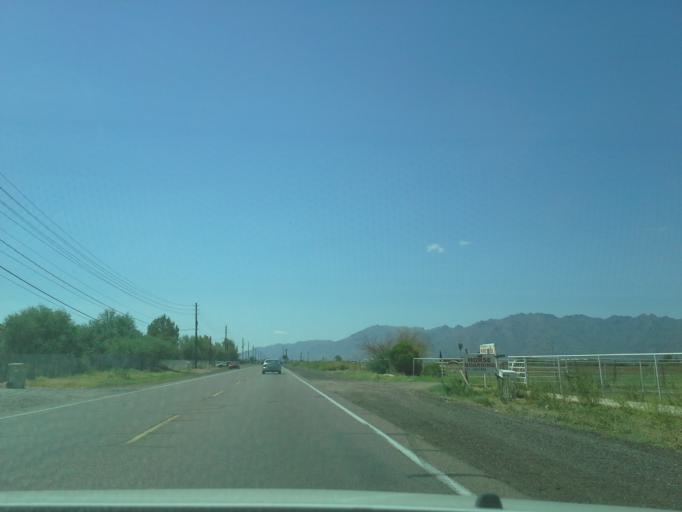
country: US
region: Arizona
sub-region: Maricopa County
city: Laveen
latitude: 33.3387
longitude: -112.1692
